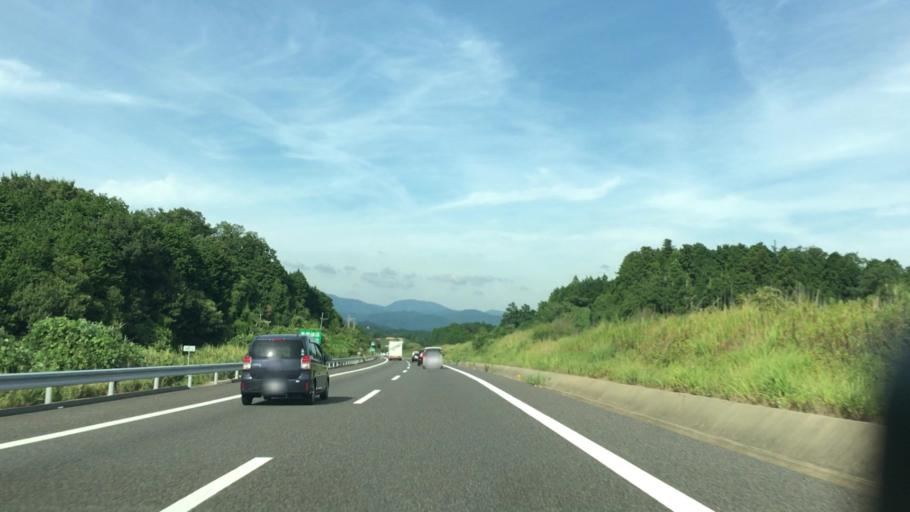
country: JP
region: Shiga Prefecture
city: Minakuchicho-matoba
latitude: 34.9173
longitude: 136.2123
